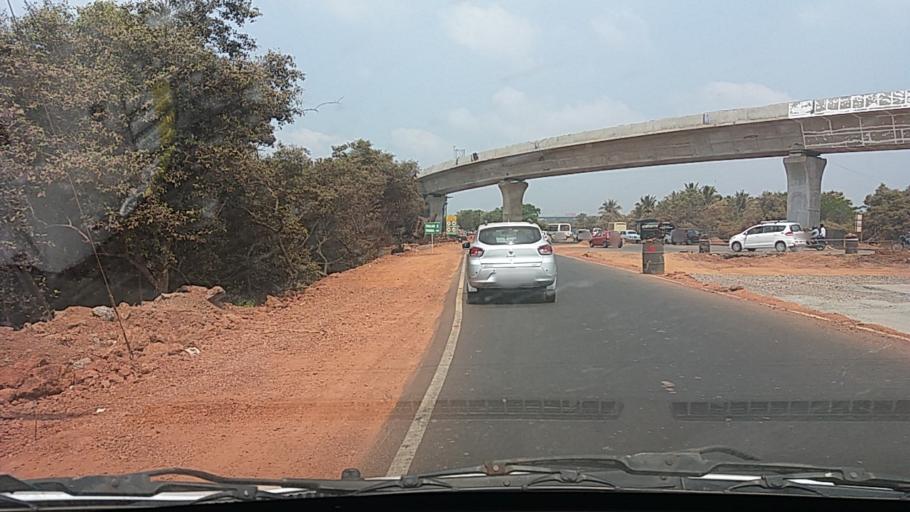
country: IN
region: Goa
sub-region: North Goa
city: Panaji
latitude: 15.4908
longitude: 73.8442
